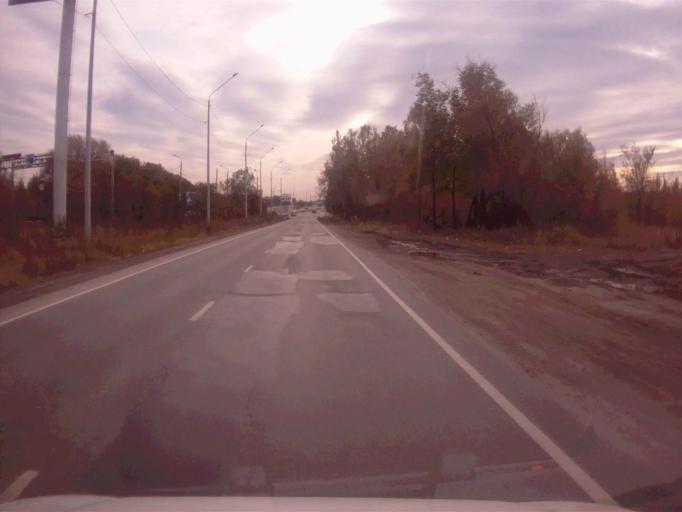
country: RU
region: Chelyabinsk
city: Novosineglazovskiy
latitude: 55.0793
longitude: 61.3880
